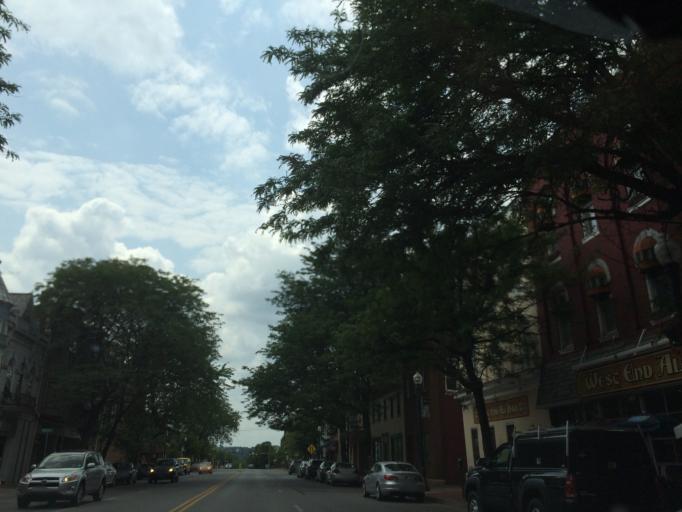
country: US
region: Pennsylvania
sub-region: Columbia County
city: Bloomsburg
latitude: 41.0023
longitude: -76.4585
